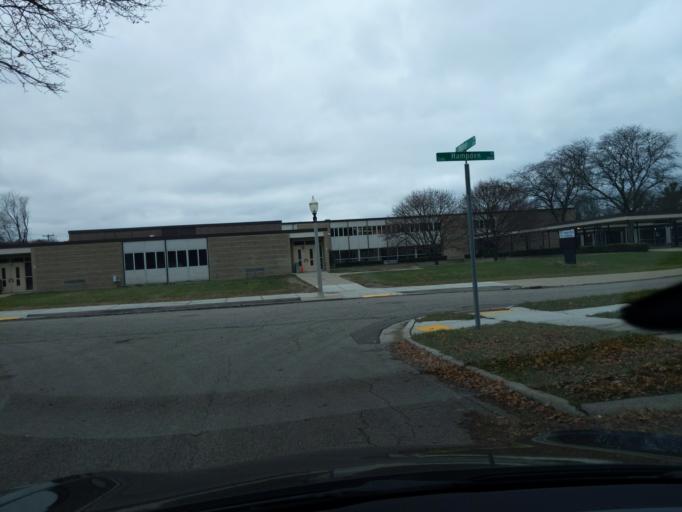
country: US
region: Michigan
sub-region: Ingham County
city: Lansing
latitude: 42.7061
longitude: -84.5833
